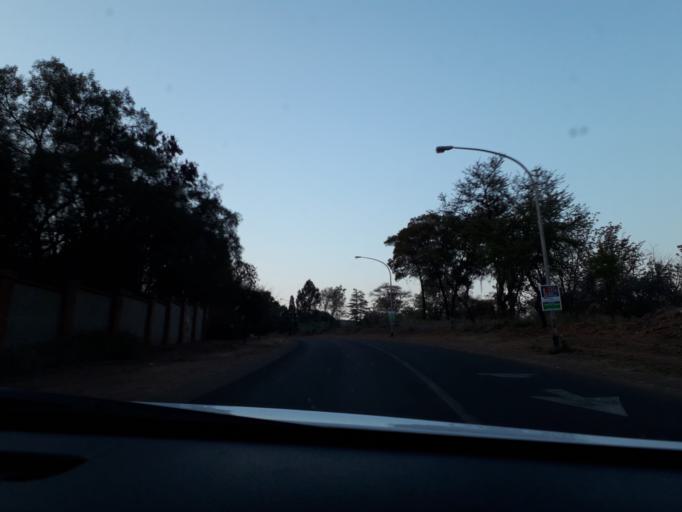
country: ZA
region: Gauteng
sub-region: City of Tshwane Metropolitan Municipality
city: Centurion
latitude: -25.8470
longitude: 28.1793
